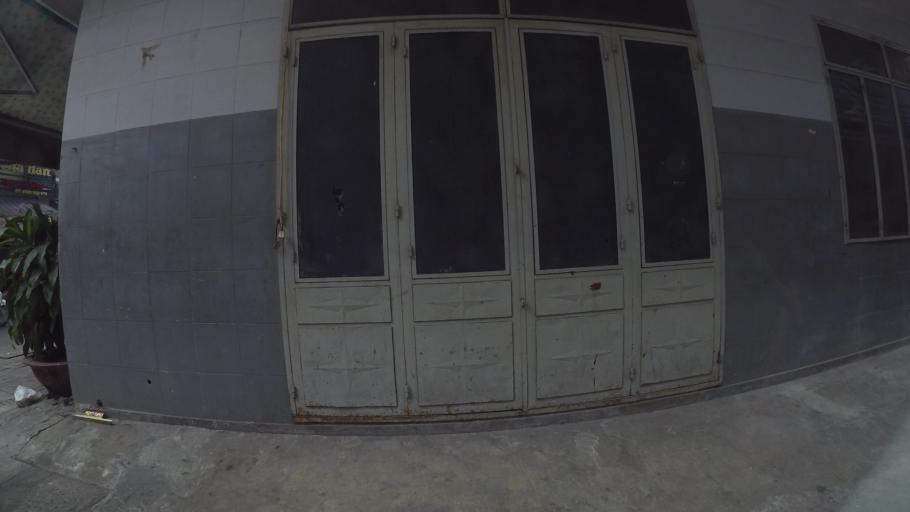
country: VN
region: Da Nang
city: Da Nang
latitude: 16.0624
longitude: 108.2139
